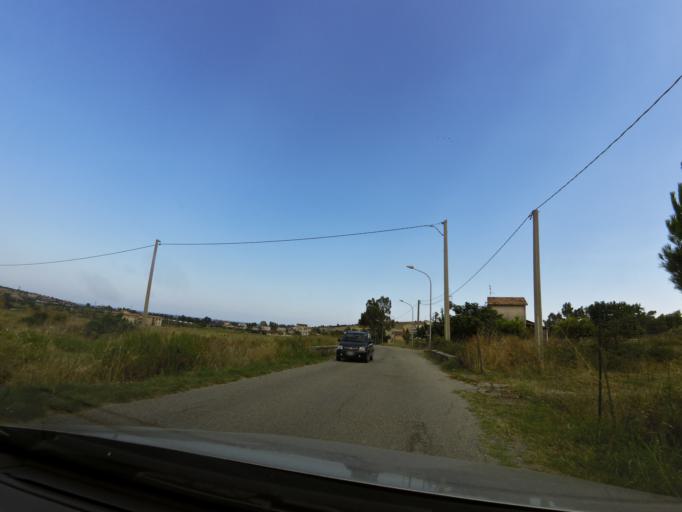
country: IT
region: Calabria
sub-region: Provincia di Reggio Calabria
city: Monasterace
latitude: 38.4242
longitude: 16.5390
